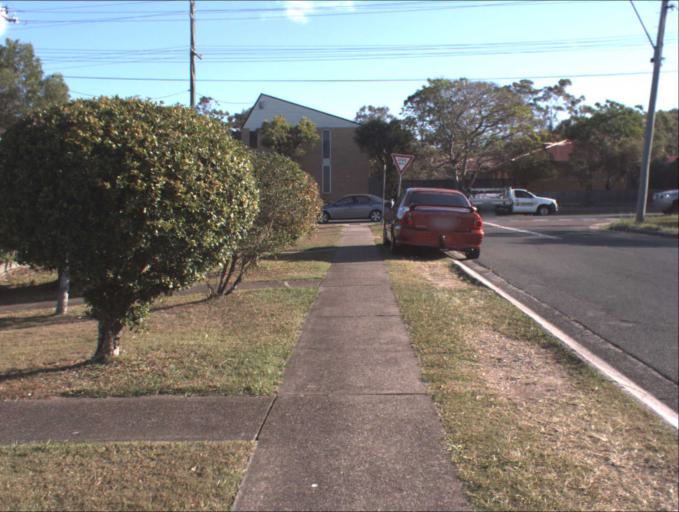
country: AU
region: Queensland
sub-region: Logan
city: Beenleigh
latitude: -27.7223
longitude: 153.2021
